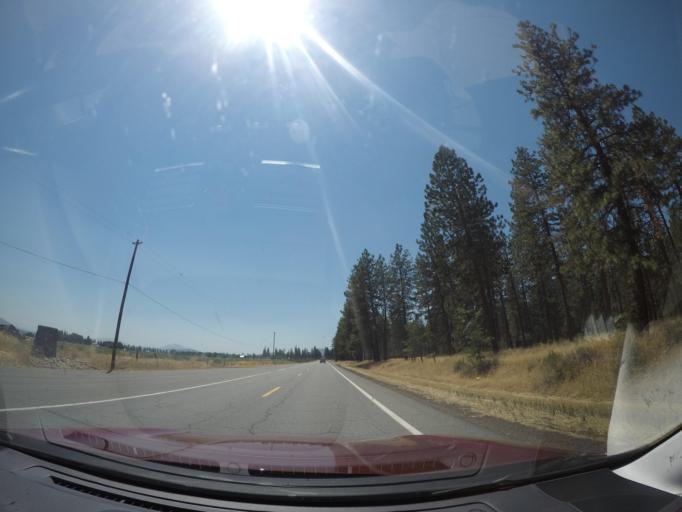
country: US
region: California
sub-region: Shasta County
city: Burney
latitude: 41.0711
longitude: -121.3374
